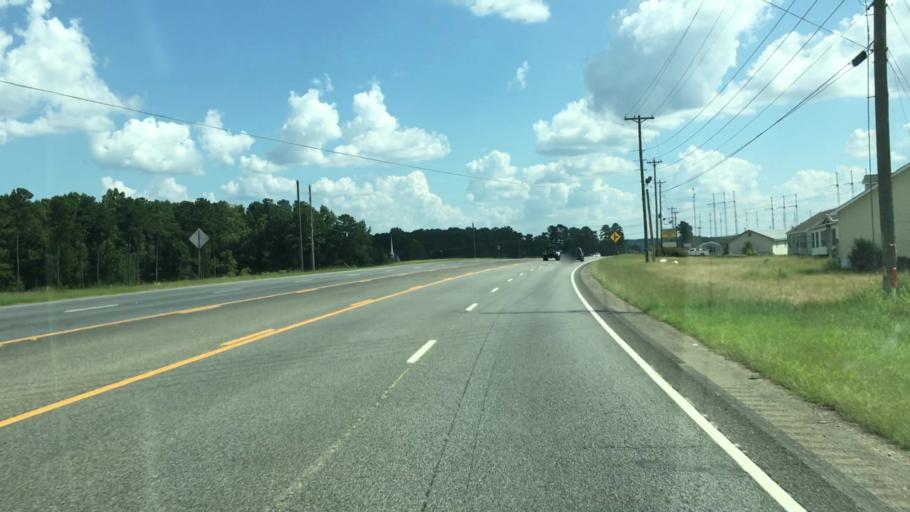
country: US
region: Georgia
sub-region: Baldwin County
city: Milledgeville
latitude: 33.2052
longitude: -83.2964
